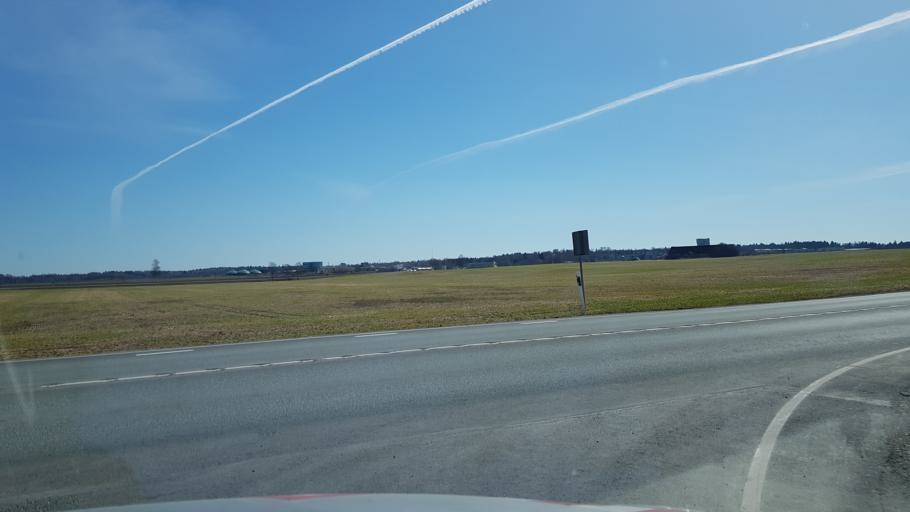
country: EE
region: Laeaene-Virumaa
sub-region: Vinni vald
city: Vinni
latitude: 59.3006
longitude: 26.4065
